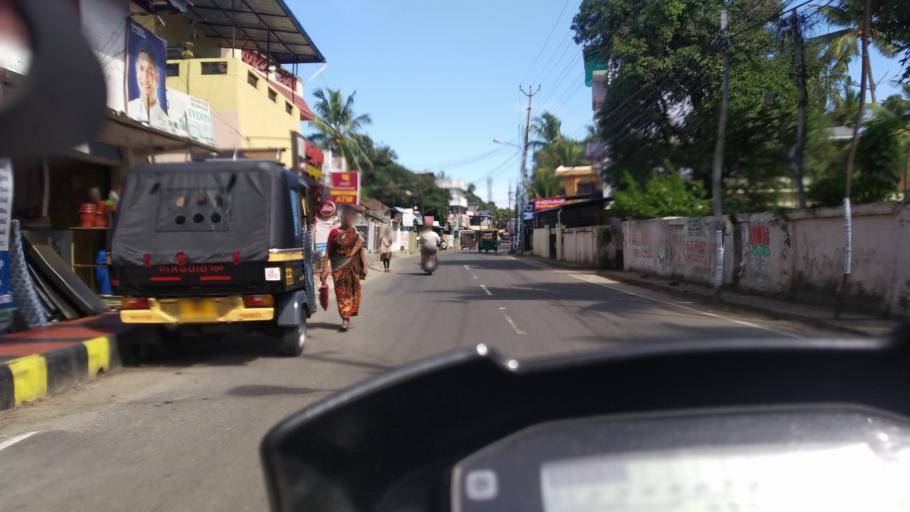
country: IN
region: Kerala
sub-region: Ernakulam
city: Elur
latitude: 10.0207
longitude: 76.2743
